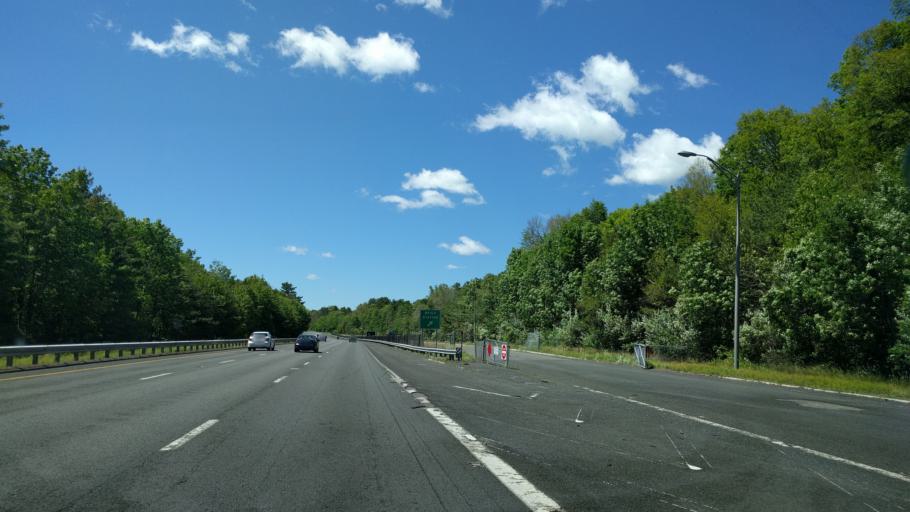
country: US
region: Massachusetts
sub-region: Hampden County
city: Holland
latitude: 42.0542
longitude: -72.1185
